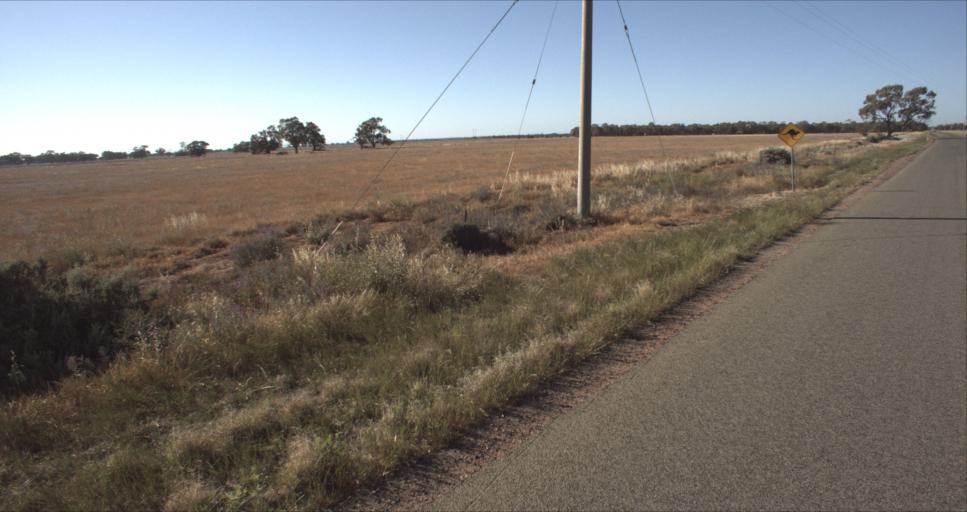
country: AU
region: New South Wales
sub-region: Leeton
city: Leeton
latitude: -34.5549
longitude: 146.2666
